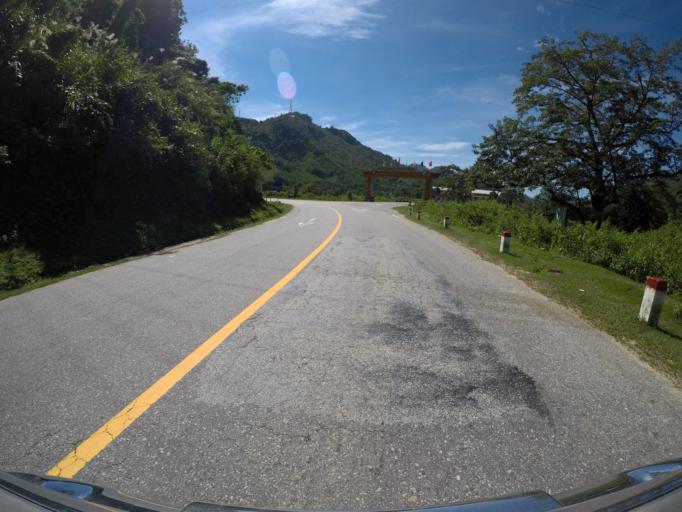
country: VN
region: Quang Nam
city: Thanh My
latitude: 15.6923
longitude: 107.7688
